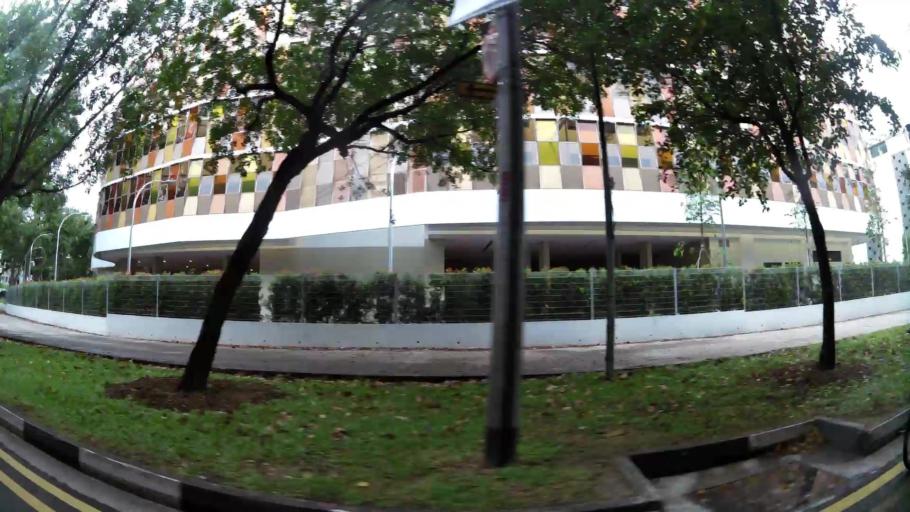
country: SG
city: Singapore
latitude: 1.2708
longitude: 103.8120
